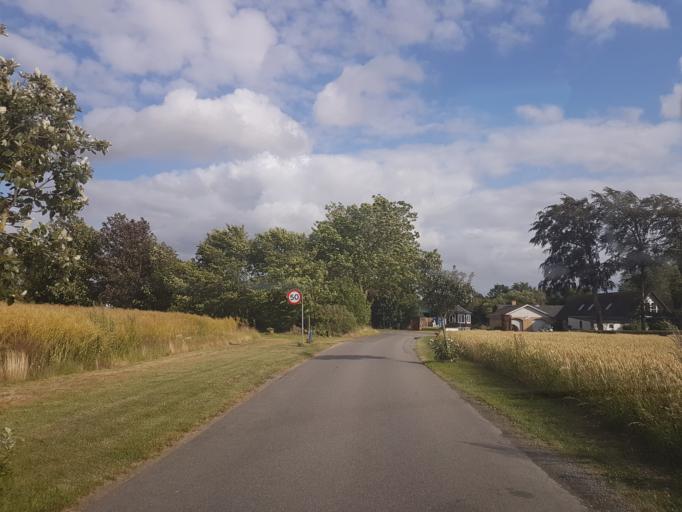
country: DK
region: South Denmark
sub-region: Middelfart Kommune
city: Brenderup
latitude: 55.5305
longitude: 10.0083
